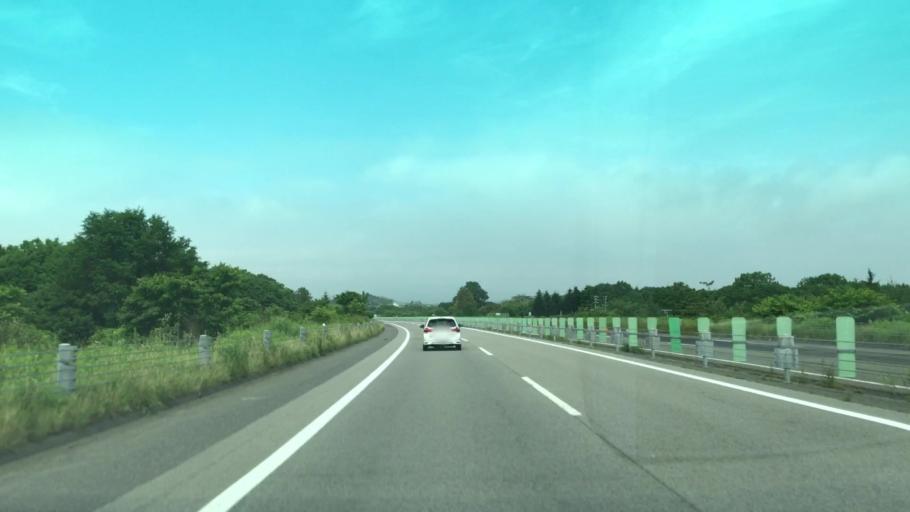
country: JP
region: Hokkaido
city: Shiraoi
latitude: 42.5062
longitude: 141.2685
